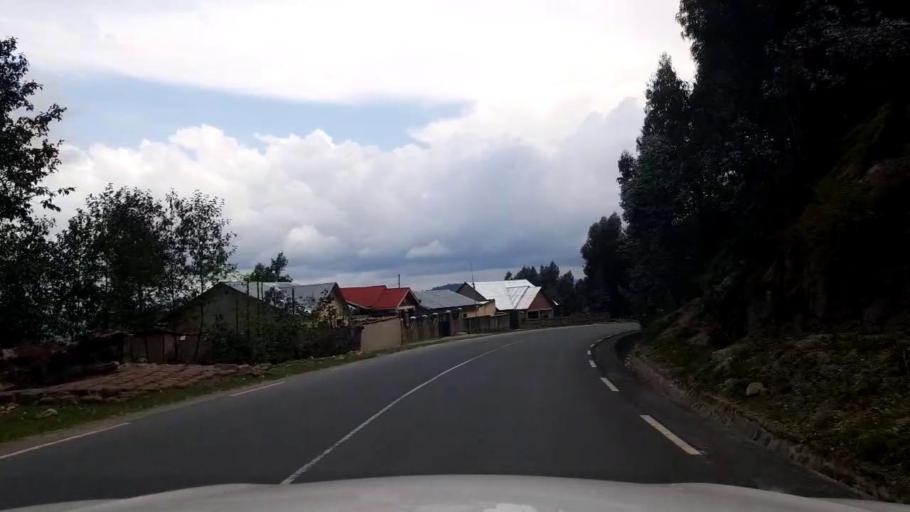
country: RW
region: Northern Province
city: Musanze
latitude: -1.6719
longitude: 29.5160
